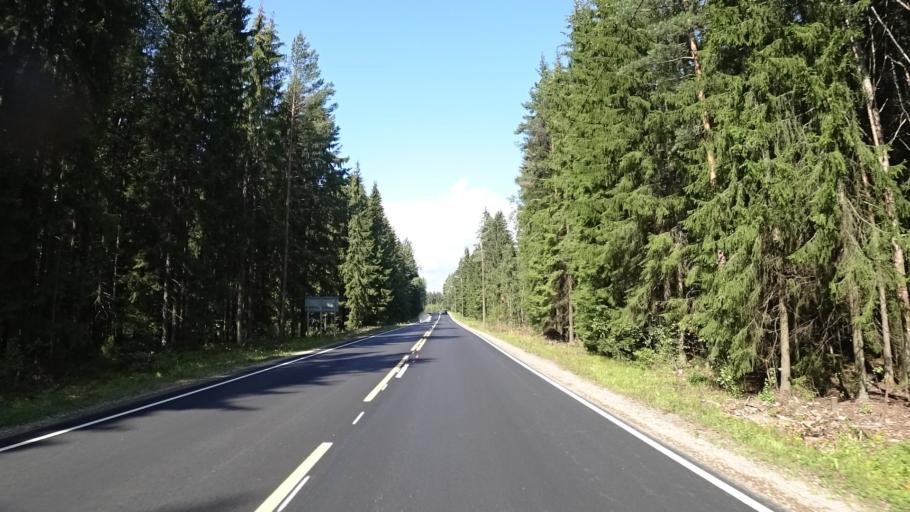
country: FI
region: Kymenlaakso
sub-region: Kotka-Hamina
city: Karhula
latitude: 60.5490
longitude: 26.9117
